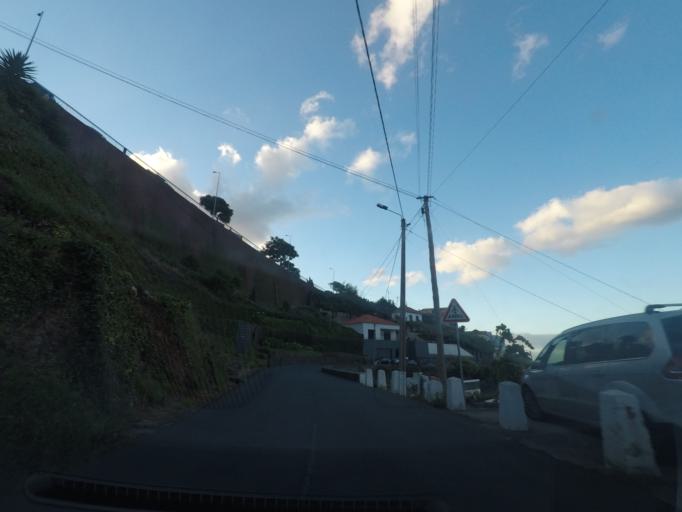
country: PT
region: Madeira
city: Camara de Lobos
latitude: 32.6708
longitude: -16.9809
